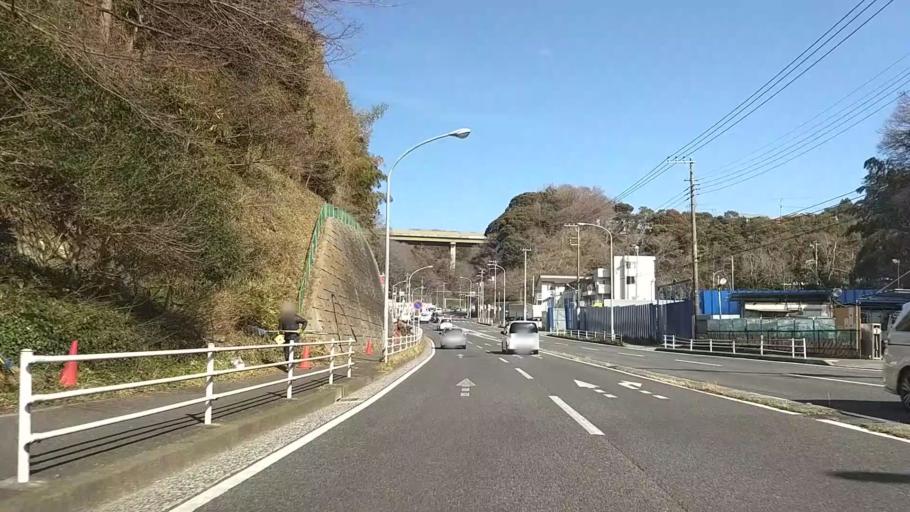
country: JP
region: Kanagawa
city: Zushi
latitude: 35.3519
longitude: 139.6069
